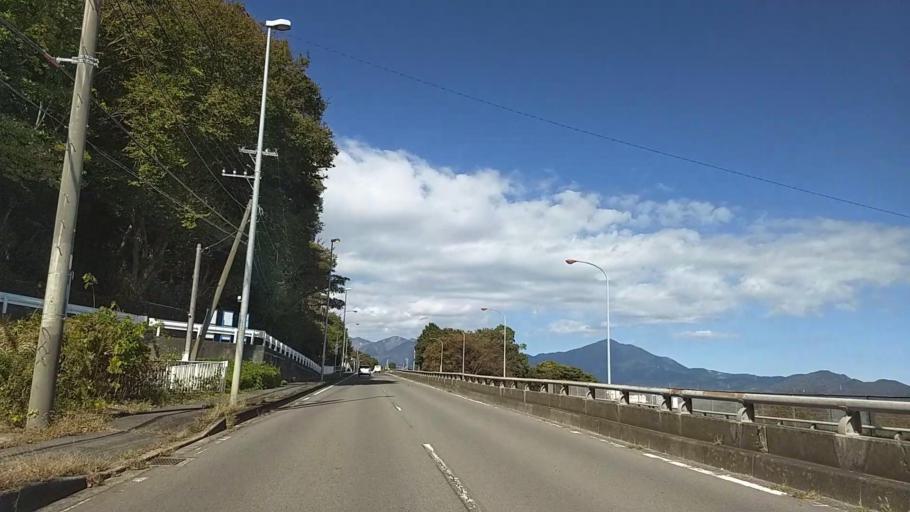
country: JP
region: Kanagawa
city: Ninomiya
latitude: 35.3320
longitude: 139.2313
